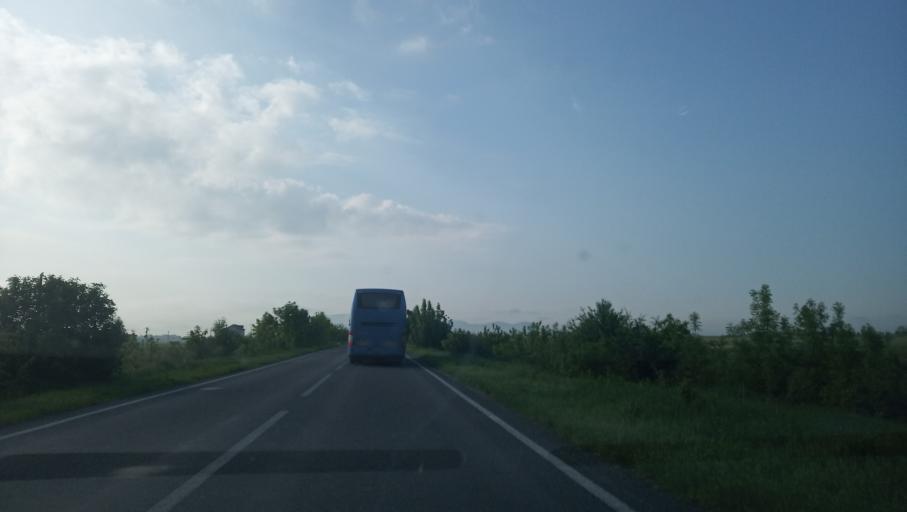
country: RO
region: Timis
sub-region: Comuna Moravita
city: Moravita
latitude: 45.2422
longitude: 21.2637
